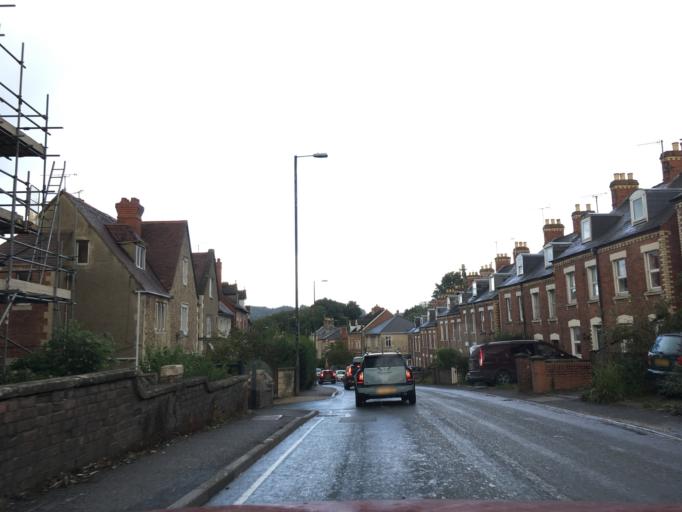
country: GB
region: England
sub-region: Gloucestershire
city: Stroud
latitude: 51.7400
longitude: -2.2299
